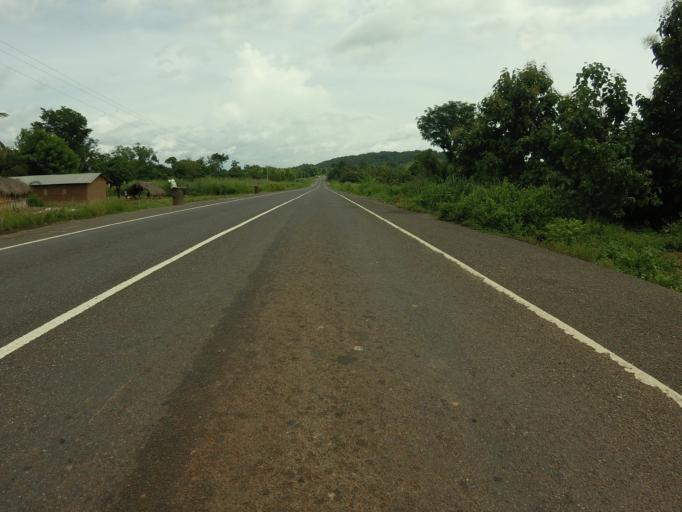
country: TG
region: Plateaux
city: Badou
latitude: 7.9519
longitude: 0.5545
